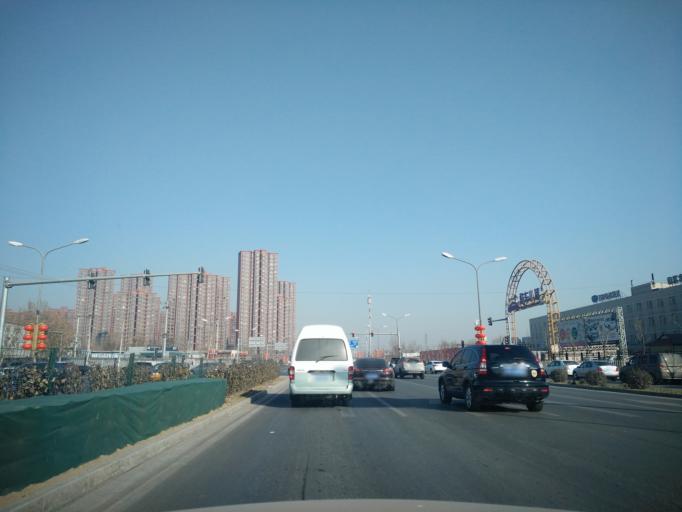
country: CN
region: Beijing
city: Dongfeng
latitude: 39.8729
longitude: 116.4949
